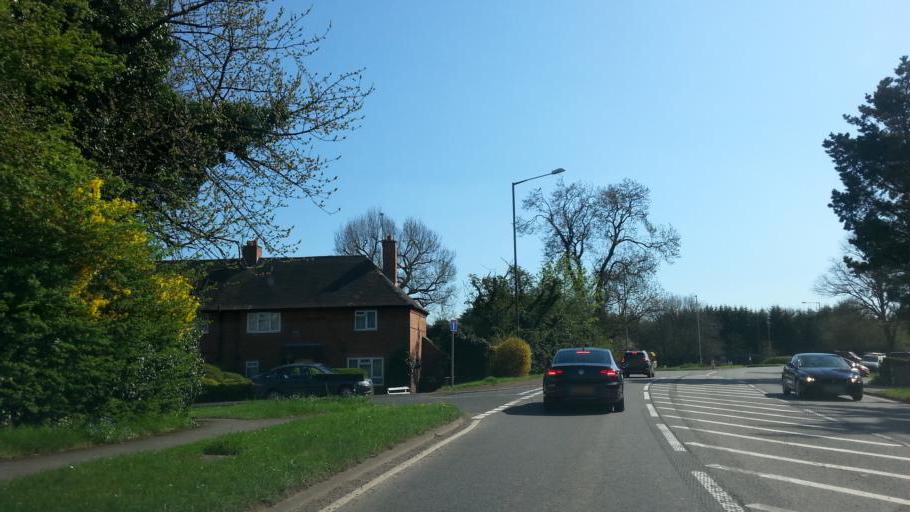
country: GB
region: England
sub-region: Worcestershire
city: Alvechurch
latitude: 52.3699
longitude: -1.9552
